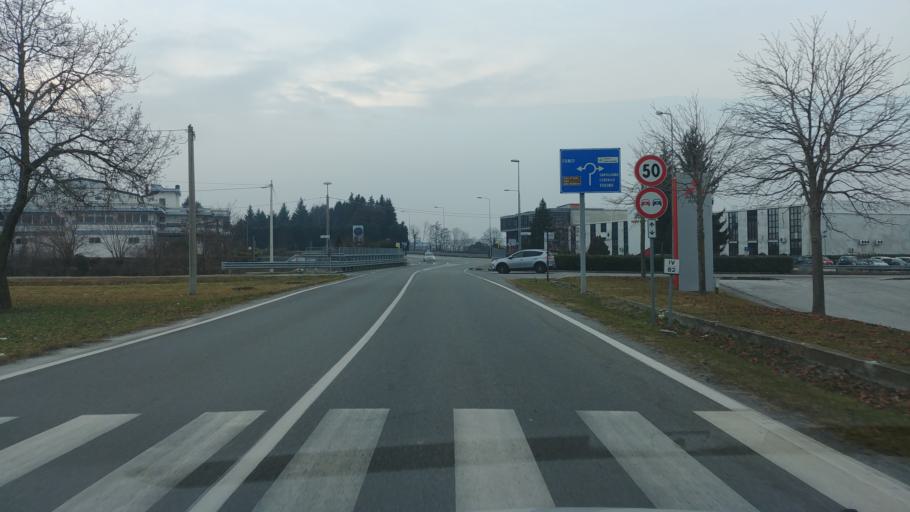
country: IT
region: Piedmont
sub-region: Provincia di Cuneo
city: Cuneo
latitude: 44.4199
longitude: 7.5582
